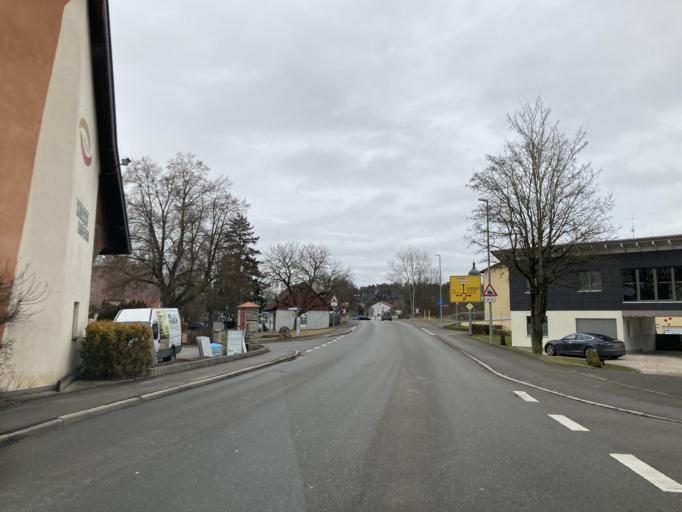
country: DE
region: Baden-Wuerttemberg
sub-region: Tuebingen Region
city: Ennetach
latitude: 48.0519
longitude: 9.3235
